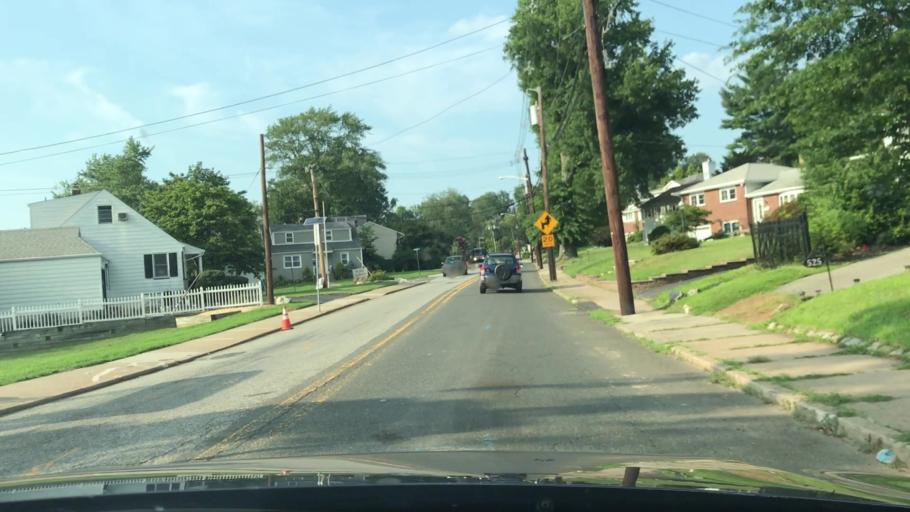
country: US
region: New Jersey
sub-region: Bergen County
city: Haworth
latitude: 40.9523
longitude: -73.9862
